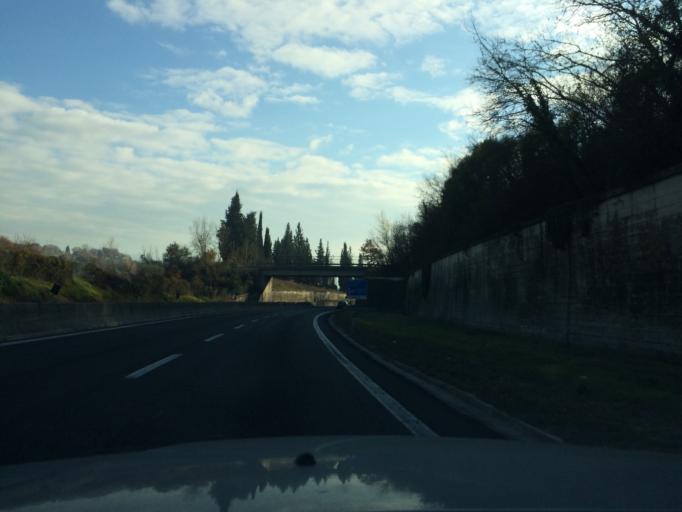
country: IT
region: Umbria
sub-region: Provincia di Terni
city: San Gemini
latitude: 42.6034
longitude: 12.5620
